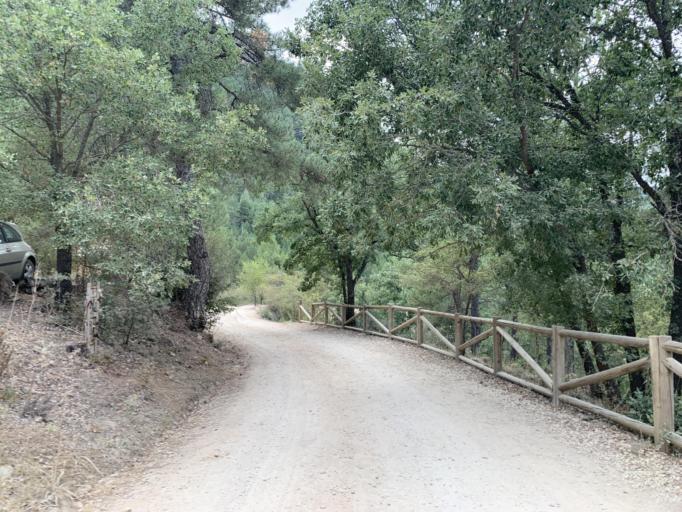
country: ES
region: Castille-La Mancha
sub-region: Provincia de Guadalajara
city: Taravilla
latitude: 40.6485
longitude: -1.9785
